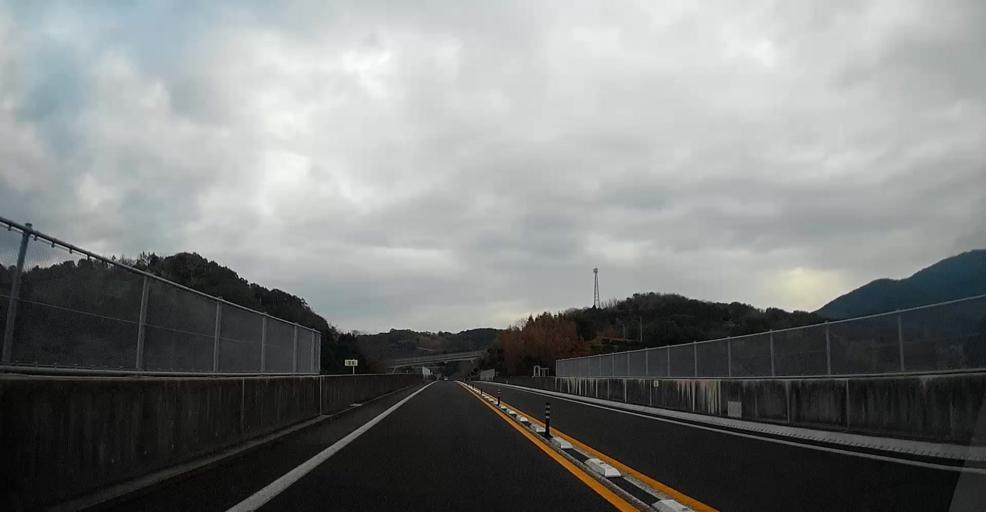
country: JP
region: Kumamoto
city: Hondo
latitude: 32.5090
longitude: 130.3275
